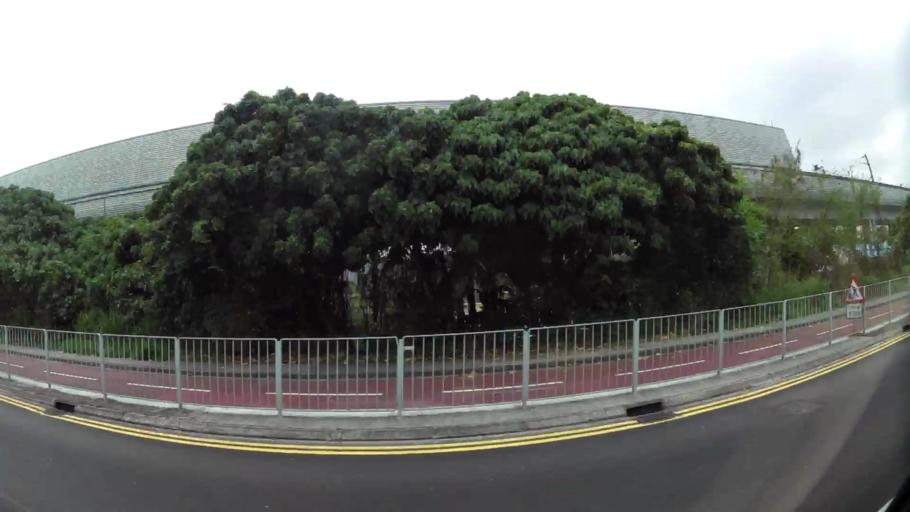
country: HK
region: Tuen Mun
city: Tuen Mun
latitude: 22.4175
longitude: 113.9817
